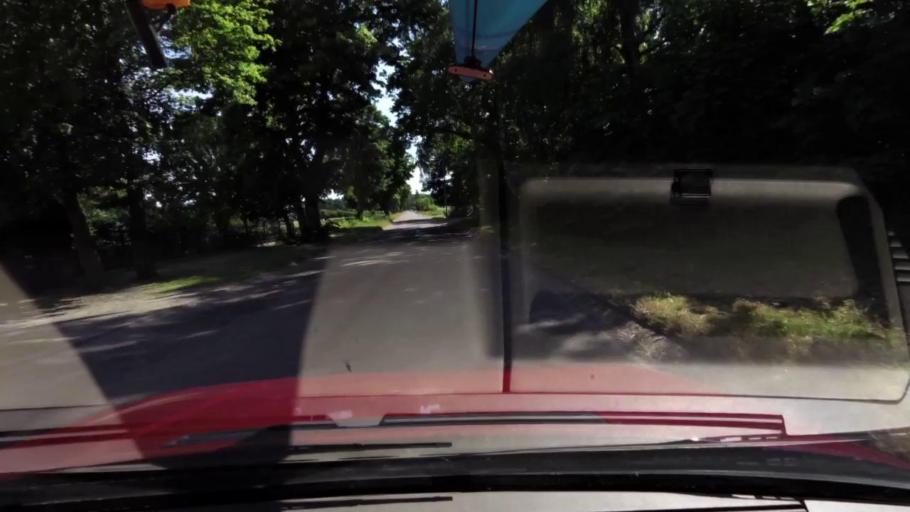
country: PL
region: Pomeranian Voivodeship
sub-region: Powiat slupski
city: Kobylnica
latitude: 54.3484
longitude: 16.9667
